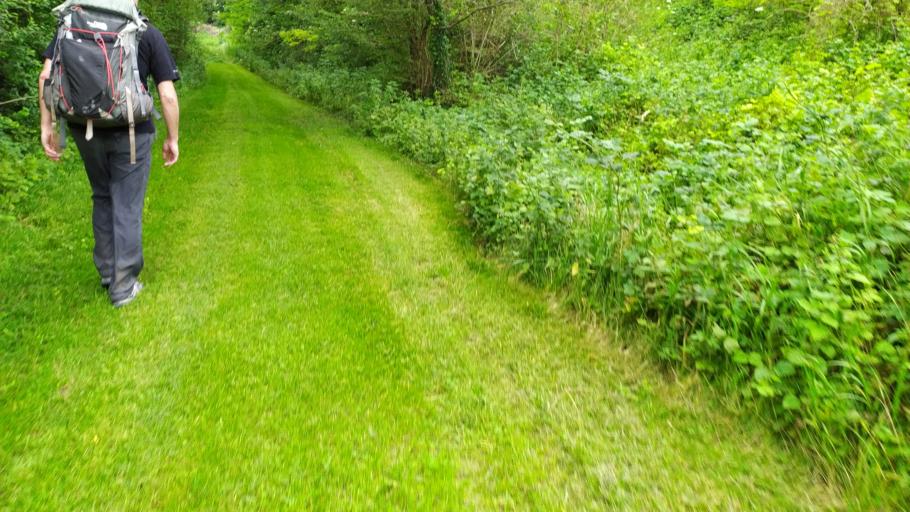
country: IT
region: Friuli Venezia Giulia
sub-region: Provincia di Udine
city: Majano
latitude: 46.1958
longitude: 13.0587
